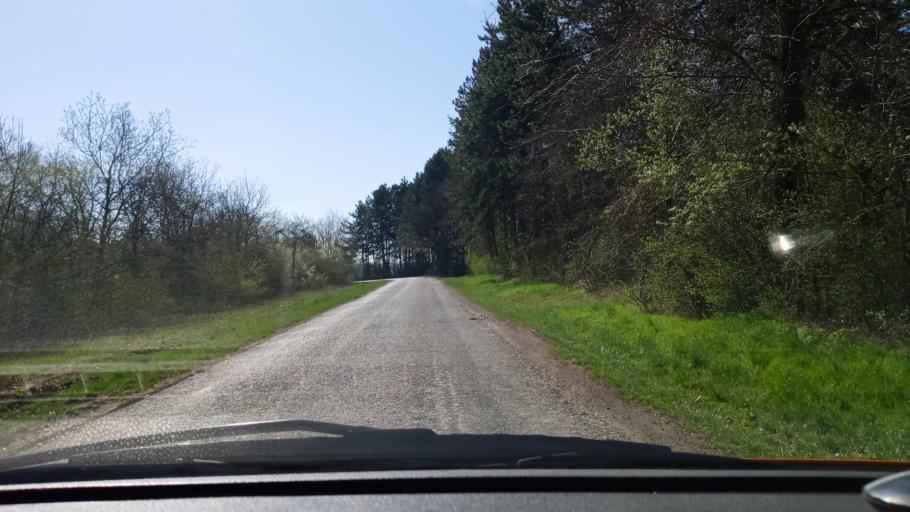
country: HU
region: Baranya
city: Kozarmisleny
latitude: 46.0773
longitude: 18.3509
